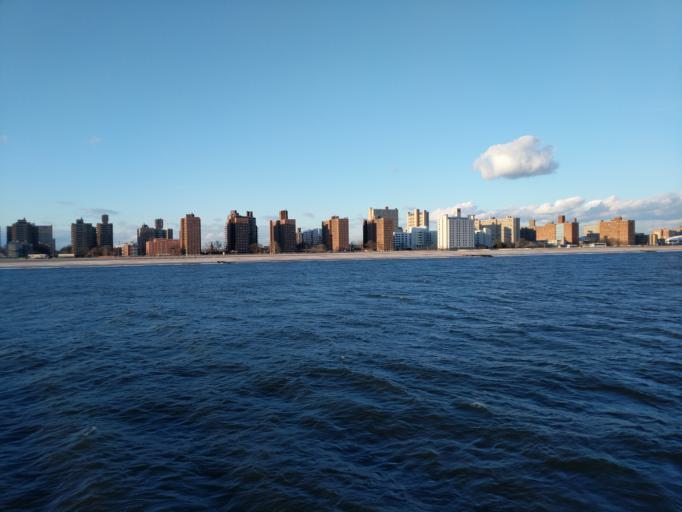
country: US
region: New York
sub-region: Kings County
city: Coney Island
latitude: 40.5671
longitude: -73.9979
